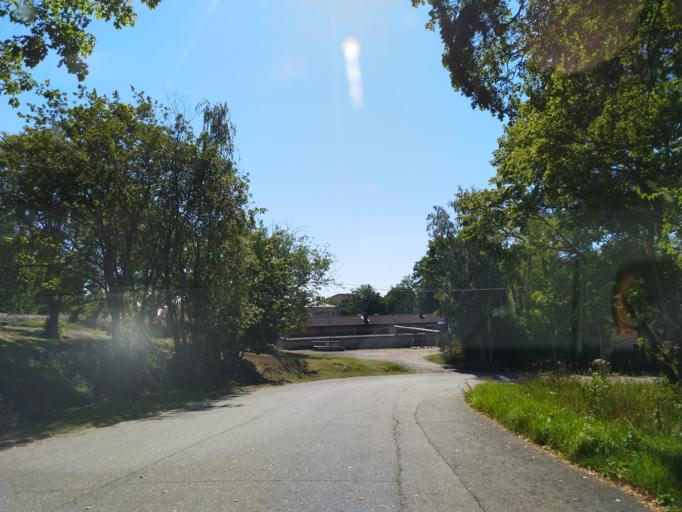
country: FI
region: Varsinais-Suomi
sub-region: Aboland-Turunmaa
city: Dragsfjaerd
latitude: 60.0221
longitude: 22.5072
